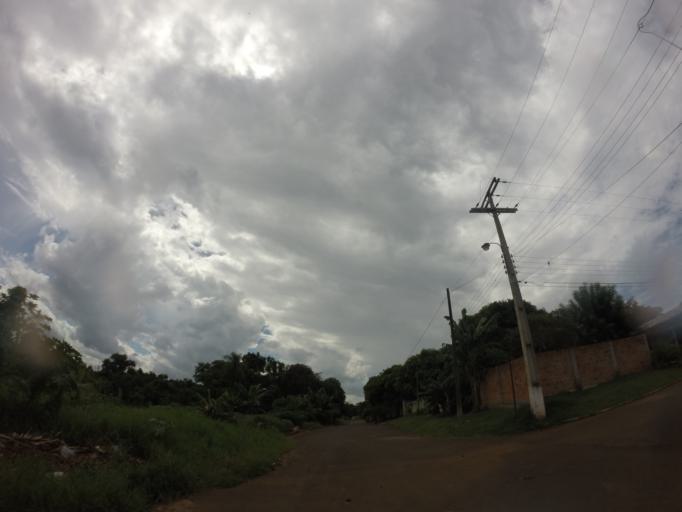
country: PY
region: Alto Parana
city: Ciudad del Este
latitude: -25.4178
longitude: -54.6294
